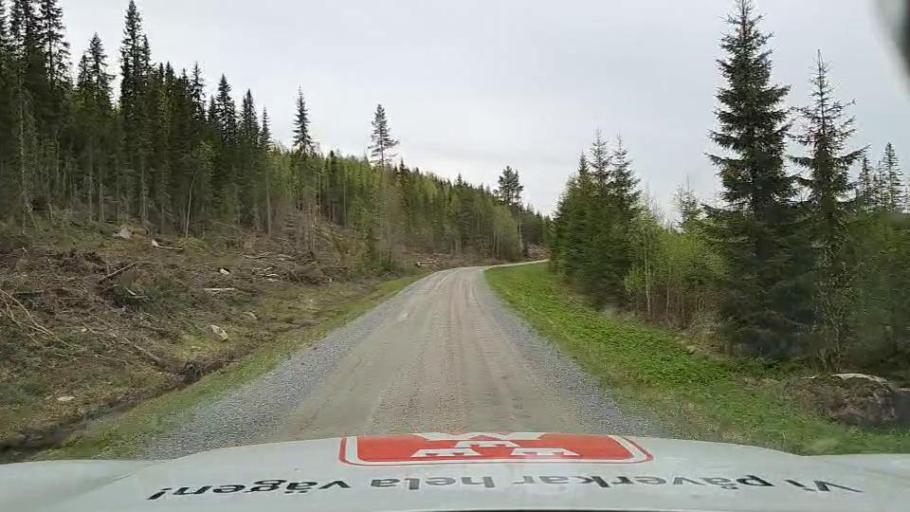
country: SE
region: Jaemtland
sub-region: Bergs Kommun
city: Hoverberg
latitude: 62.5563
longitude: 14.6892
